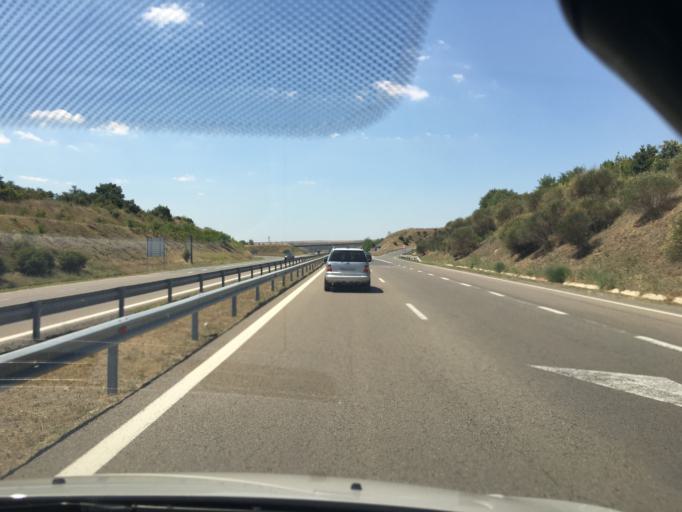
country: BG
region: Burgas
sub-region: Obshtina Karnobat
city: Karnobat
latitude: 42.5906
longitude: 26.9894
